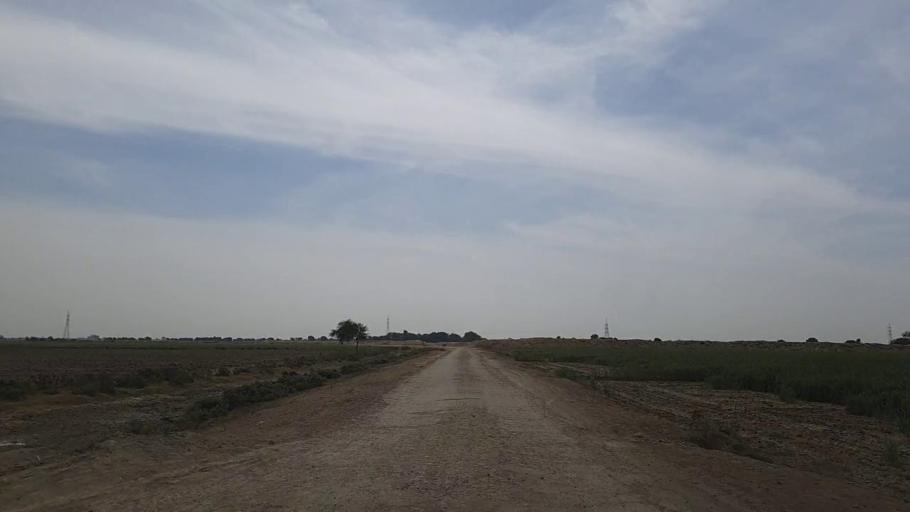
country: PK
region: Sindh
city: Samaro
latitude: 25.2988
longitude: 69.4528
